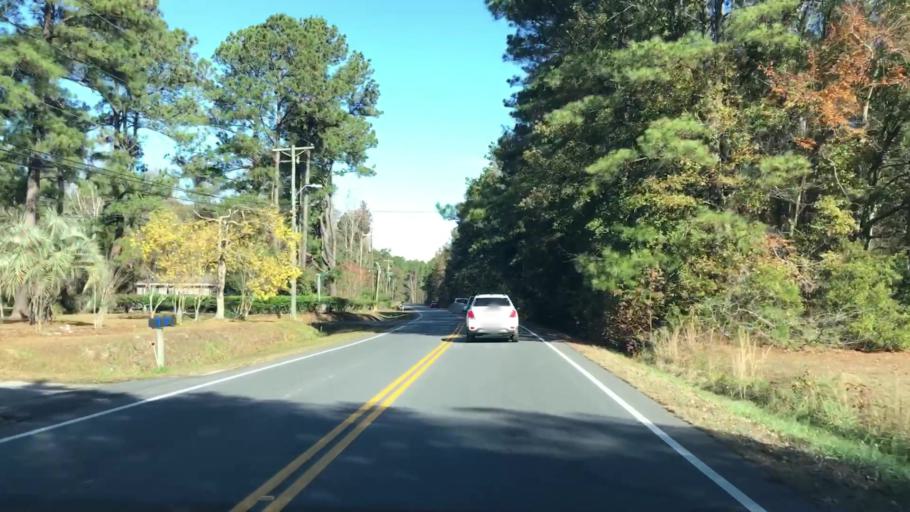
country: US
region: South Carolina
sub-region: Dorchester County
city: Summerville
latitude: 33.0187
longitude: -80.2043
